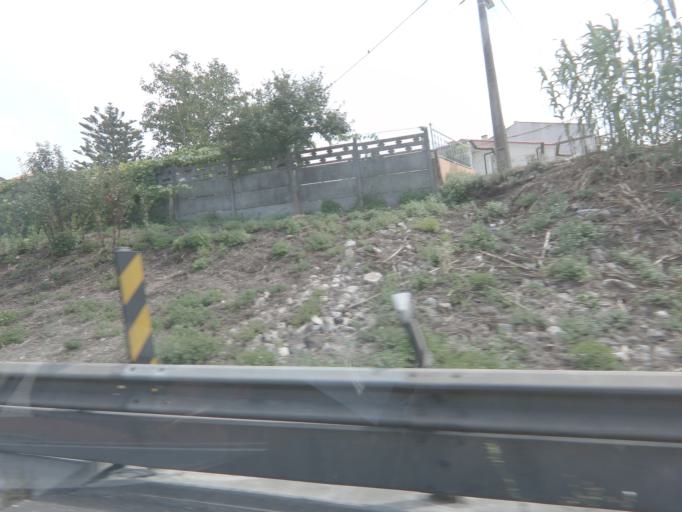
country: PT
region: Leiria
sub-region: Leiria
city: Leiria
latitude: 39.7618
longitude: -8.7984
